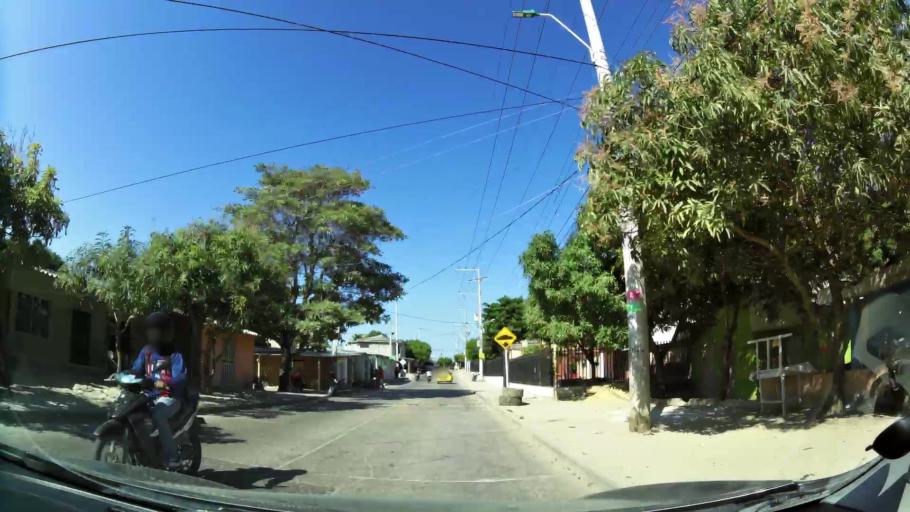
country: CO
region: Atlantico
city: Barranquilla
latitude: 10.9328
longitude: -74.8119
